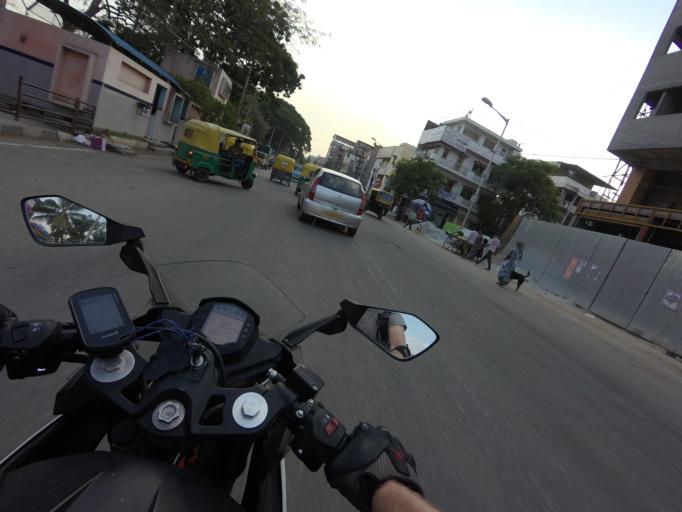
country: IN
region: Karnataka
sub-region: Bangalore Urban
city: Bangalore
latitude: 13.0175
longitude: 77.6363
